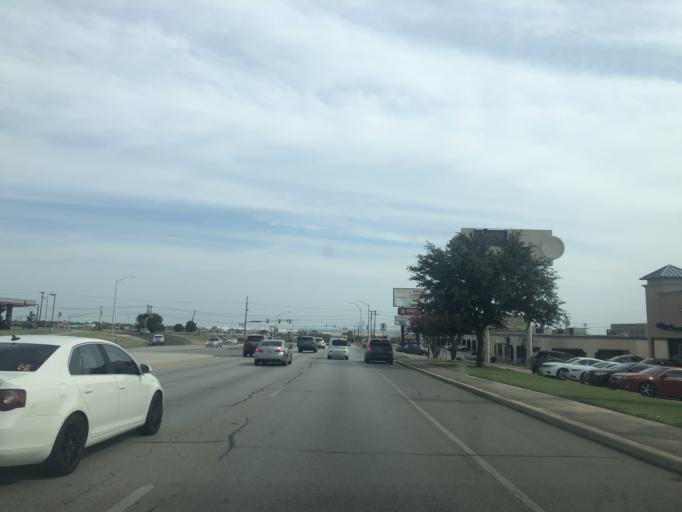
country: US
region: Texas
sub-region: Tarrant County
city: White Settlement
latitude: 32.7322
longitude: -97.4406
